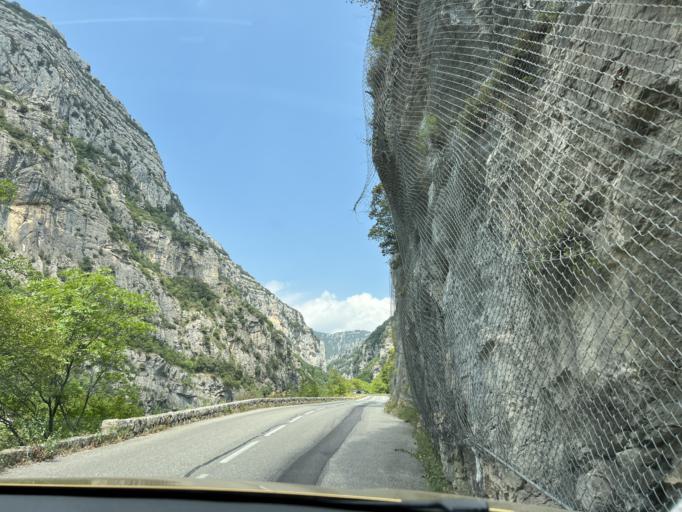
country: FR
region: Provence-Alpes-Cote d'Azur
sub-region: Departement des Alpes-Maritimes
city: Le Rouret
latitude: 43.7288
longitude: 6.9971
